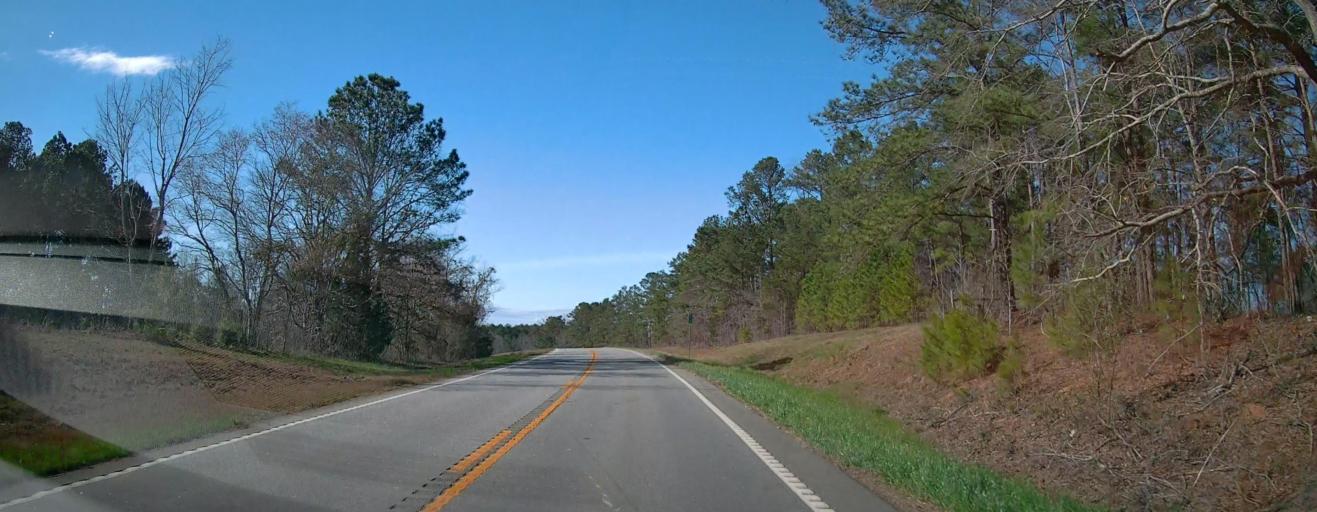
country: US
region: Georgia
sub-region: Macon County
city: Oglethorpe
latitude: 32.3428
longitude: -84.1336
